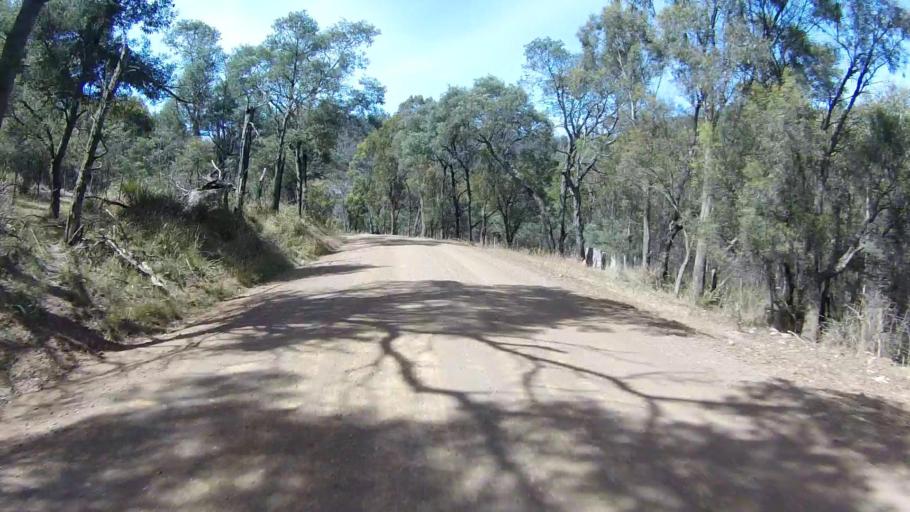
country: AU
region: Tasmania
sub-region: Sorell
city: Sorell
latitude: -42.6357
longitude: 147.7248
